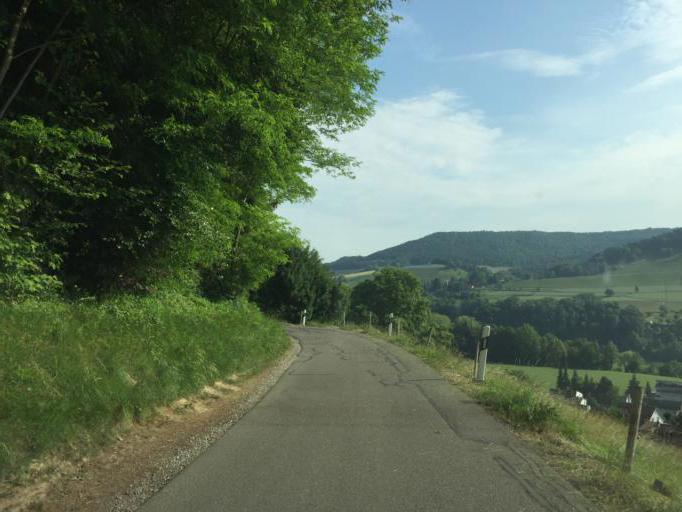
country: CH
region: Zurich
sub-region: Bezirk Buelach
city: Rorbas
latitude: 47.5323
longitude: 8.5678
